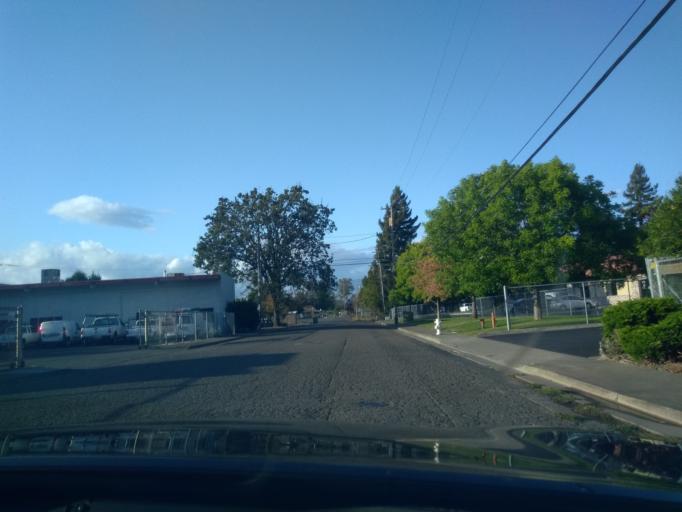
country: US
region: California
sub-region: Mendocino County
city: Ukiah
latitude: 39.1610
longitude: -123.2073
